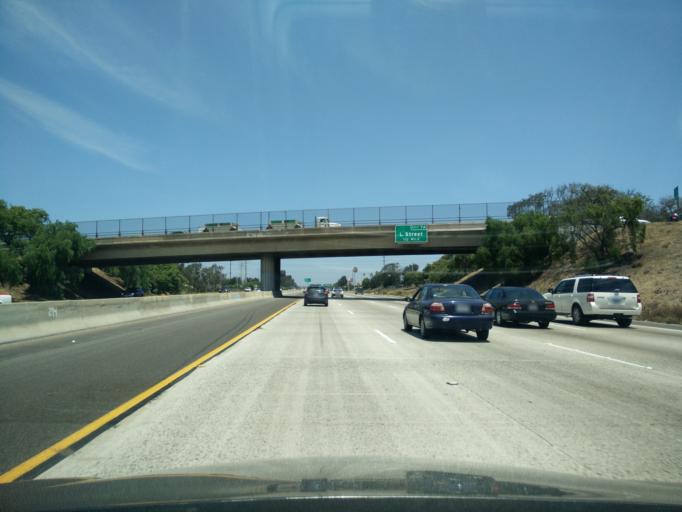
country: US
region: California
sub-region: San Diego County
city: Imperial Beach
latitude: 32.6036
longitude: -117.0898
